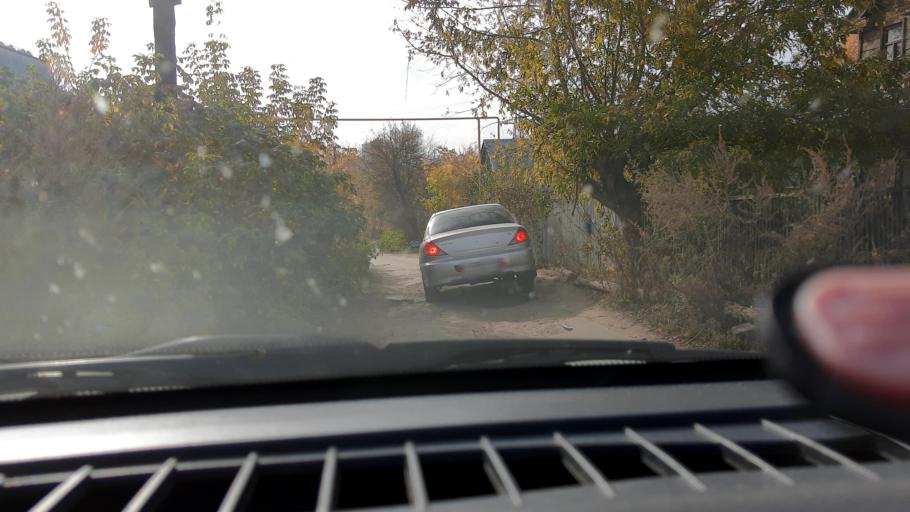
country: RU
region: Nizjnij Novgorod
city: Nizhniy Novgorod
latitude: 56.3113
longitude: 44.0446
